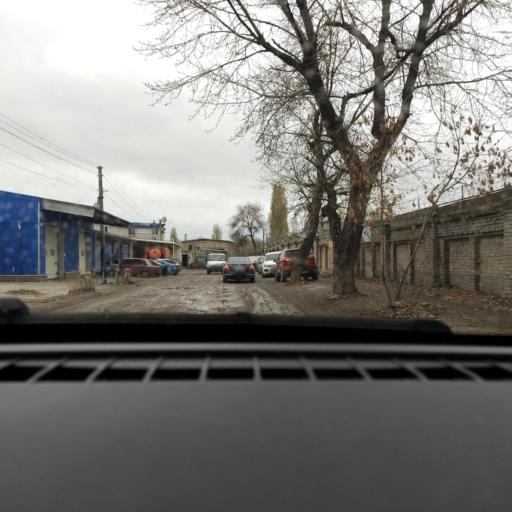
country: RU
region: Voronezj
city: Voronezh
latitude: 51.6247
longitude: 39.2301
